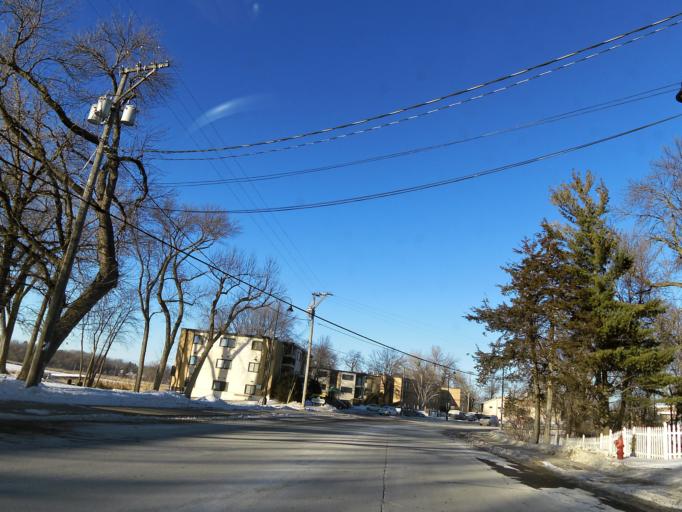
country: US
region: Minnesota
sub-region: Hennepin County
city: Mound
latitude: 44.9324
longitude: -93.6691
